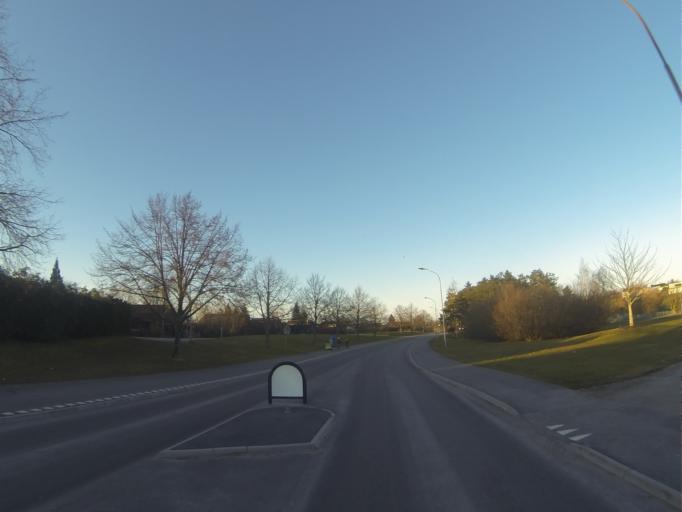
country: SE
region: Skane
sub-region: Staffanstorps Kommun
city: Staffanstorp
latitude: 55.5839
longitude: 13.1802
